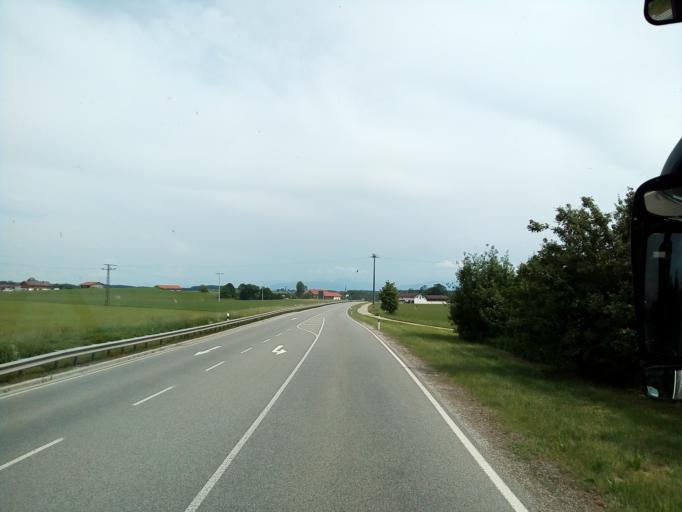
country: DE
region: Bavaria
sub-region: Upper Bavaria
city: Obing
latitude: 48.0160
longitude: 12.3844
